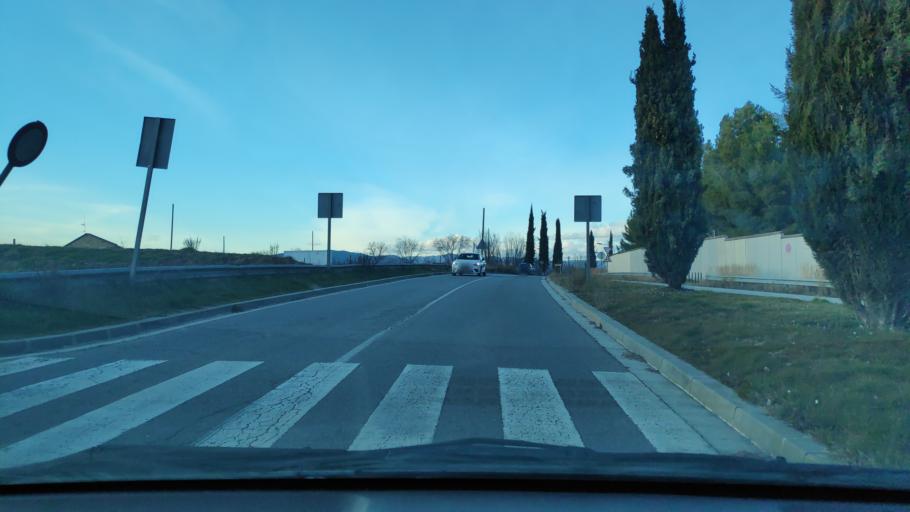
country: ES
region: Catalonia
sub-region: Provincia de Barcelona
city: Montmelo
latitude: 41.5638
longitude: 2.2519
